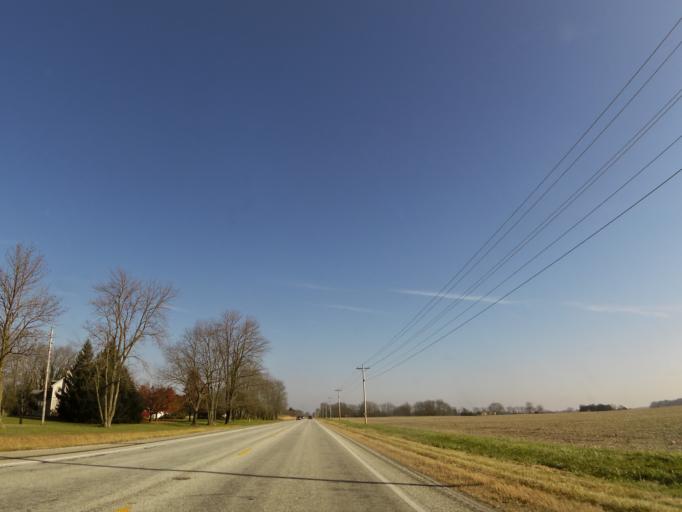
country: US
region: Indiana
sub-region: Shelby County
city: Shelbyville
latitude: 39.5371
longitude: -85.7108
